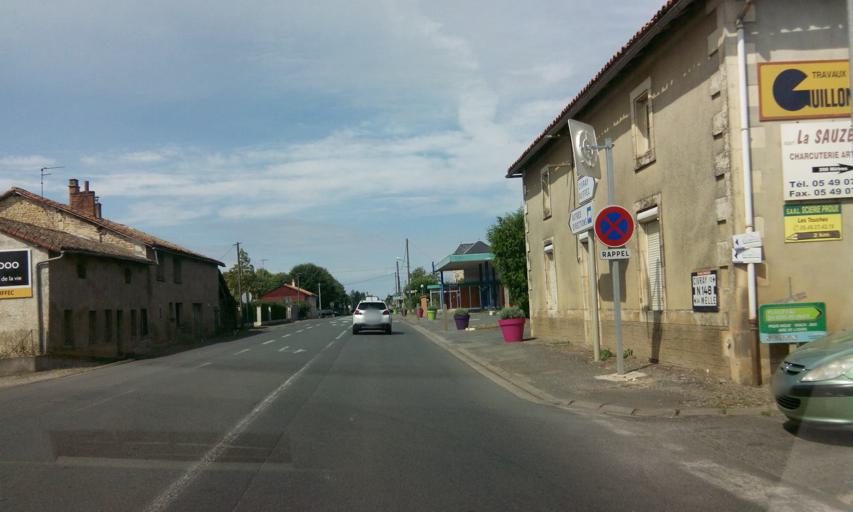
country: FR
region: Poitou-Charentes
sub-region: Departement des Deux-Sevres
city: Sauze-Vaussais
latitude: 46.1340
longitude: 0.1167
